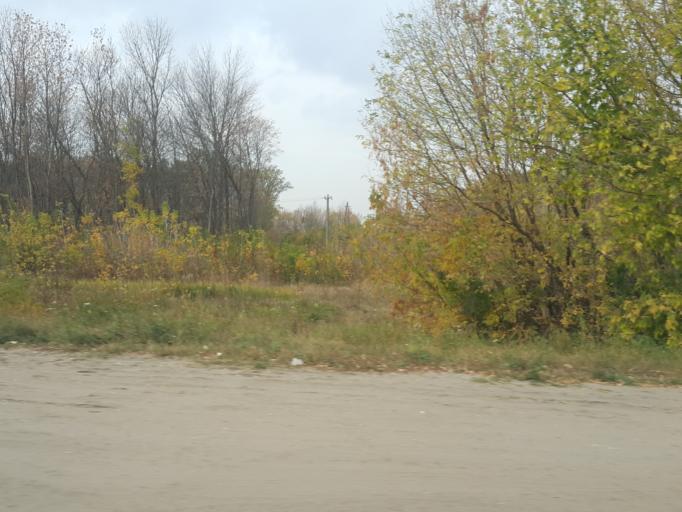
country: RU
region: Tambov
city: Bokino
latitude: 52.6400
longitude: 41.4399
